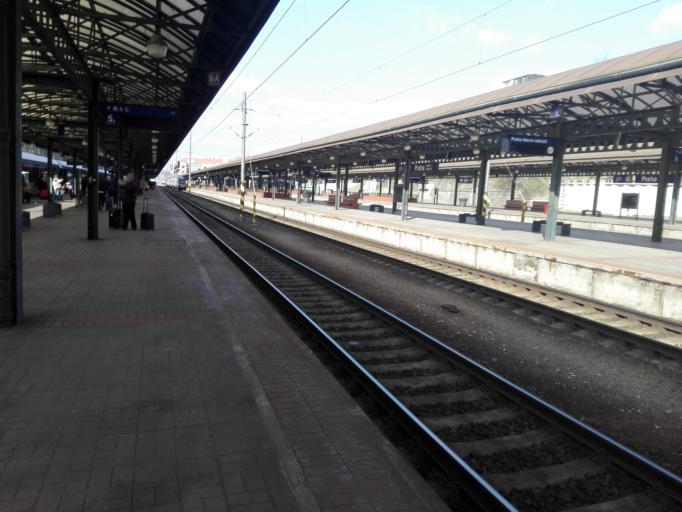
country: CZ
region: Praha
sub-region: Praha 8
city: Karlin
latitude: 50.0815
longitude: 14.4358
